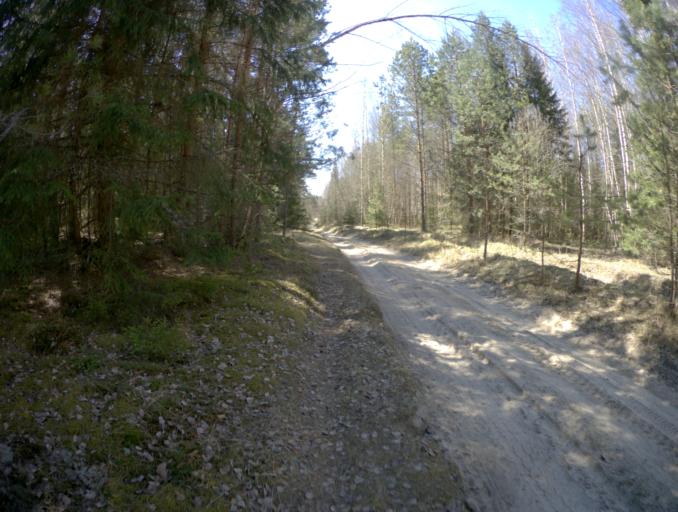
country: RU
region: Vladimir
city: Golovino
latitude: 55.8980
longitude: 40.4254
